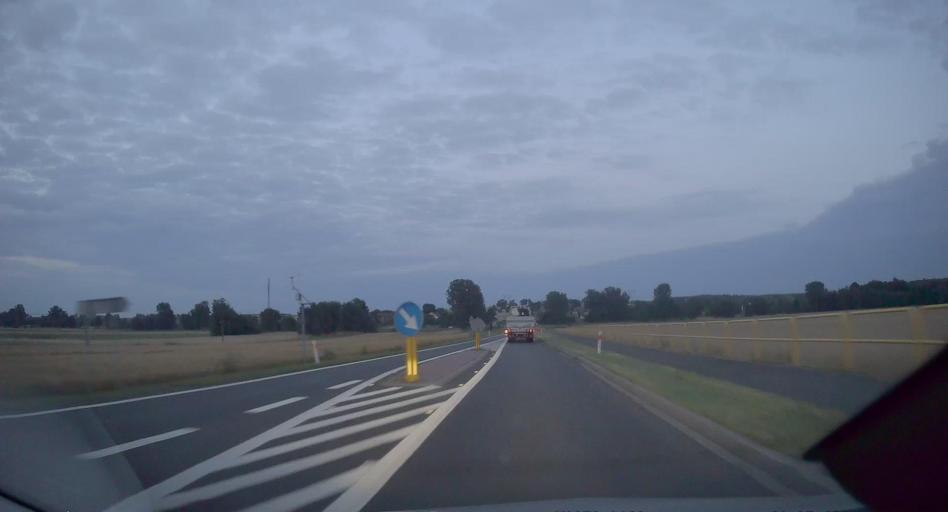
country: PL
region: Silesian Voivodeship
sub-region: Powiat klobucki
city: Opatow
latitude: 50.9529
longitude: 18.8088
